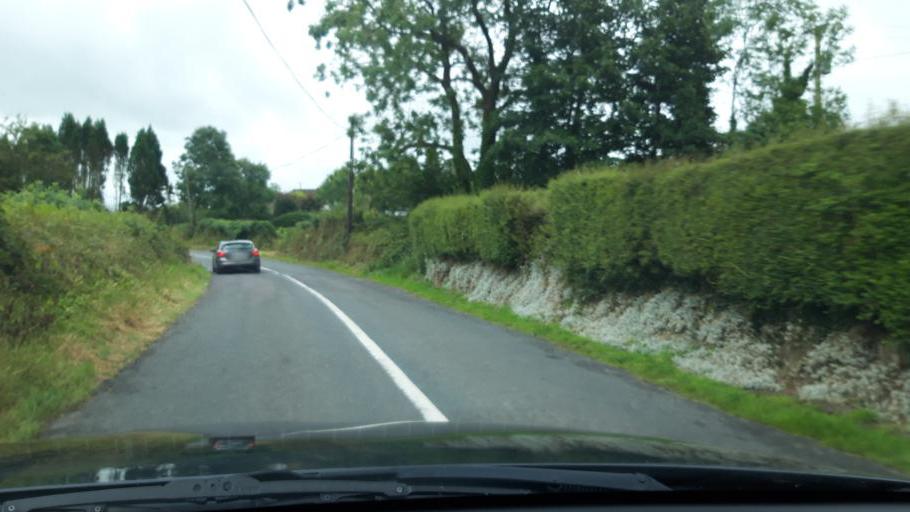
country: IE
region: Munster
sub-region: County Cork
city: Youghal
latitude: 52.1607
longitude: -7.8464
